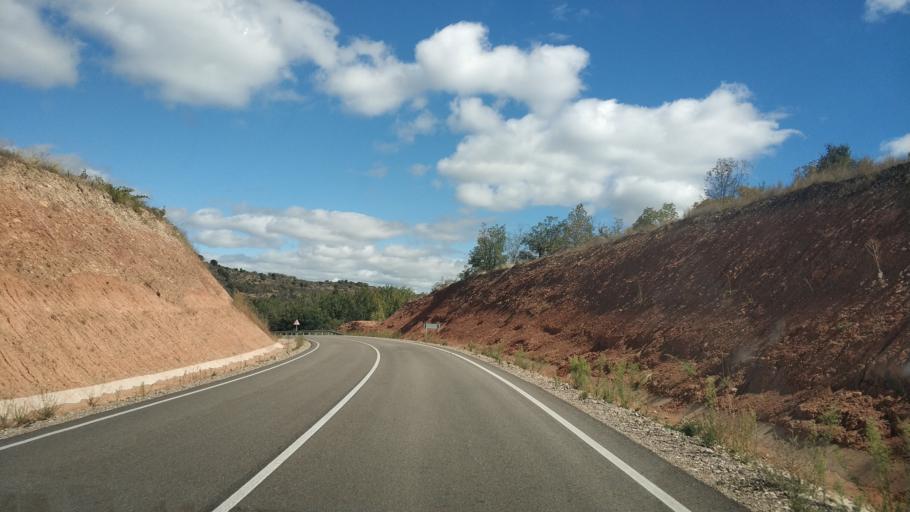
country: ES
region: Castille and Leon
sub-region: Provincia de Burgos
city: Covarrubias
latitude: 42.0460
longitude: -3.5463
